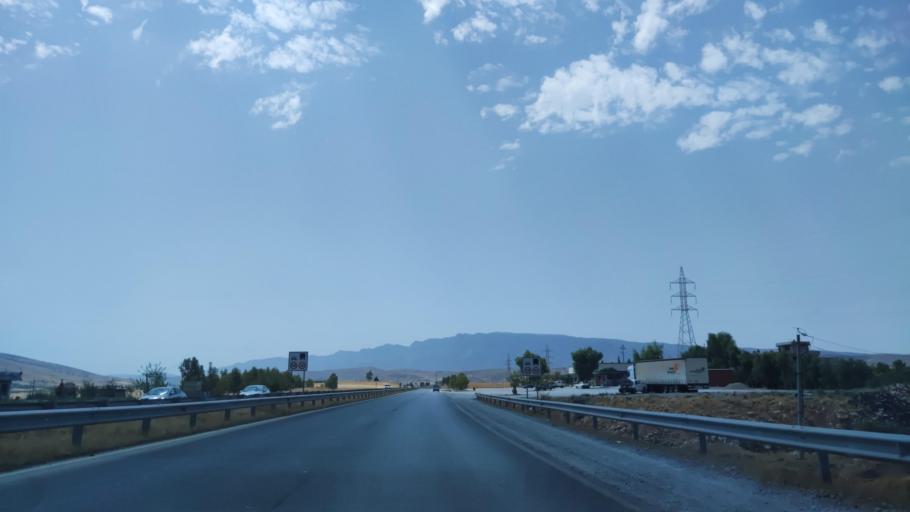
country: IQ
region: Arbil
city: Shaqlawah
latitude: 36.4844
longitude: 44.3812
